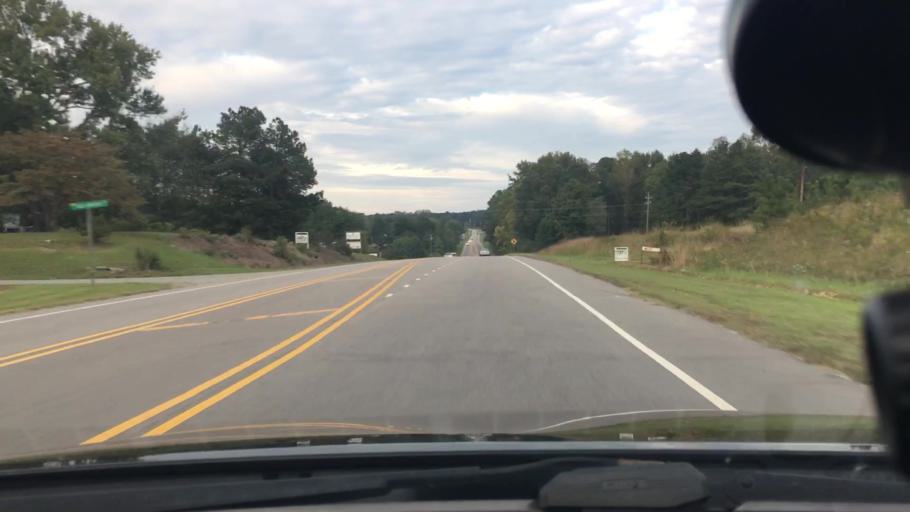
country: US
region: North Carolina
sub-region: Lee County
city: Sanford
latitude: 35.3959
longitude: -79.2423
